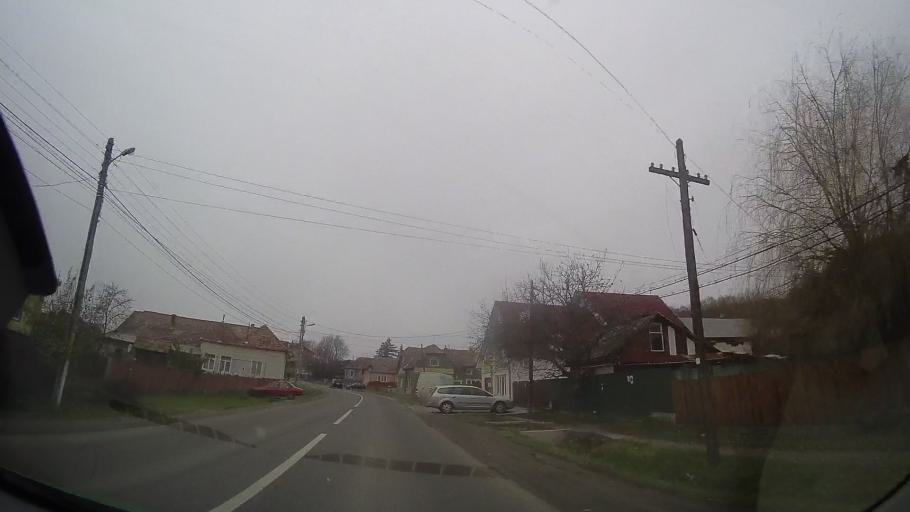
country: RO
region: Mures
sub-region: Comuna Ceausu de Campie
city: Ceausu de Campie
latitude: 46.6422
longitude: 24.5128
